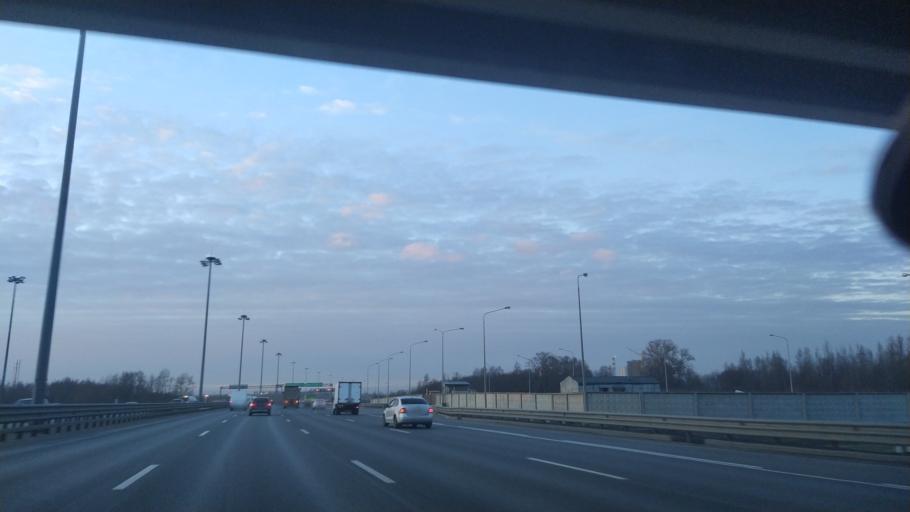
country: RU
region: St.-Petersburg
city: Krasnogvargeisky
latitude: 59.9904
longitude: 30.4833
